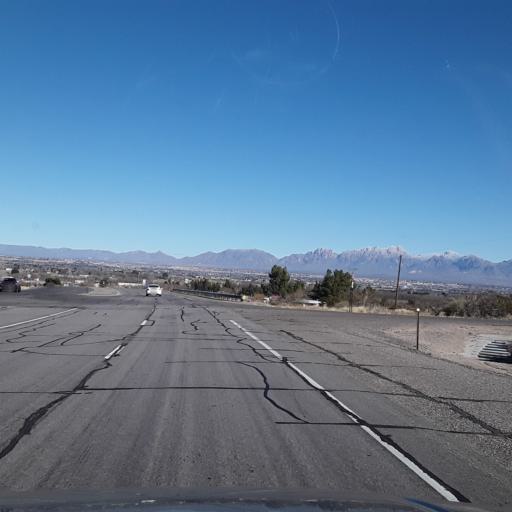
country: US
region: New Mexico
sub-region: Dona Ana County
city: Mesilla
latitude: 32.2936
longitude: -106.8610
